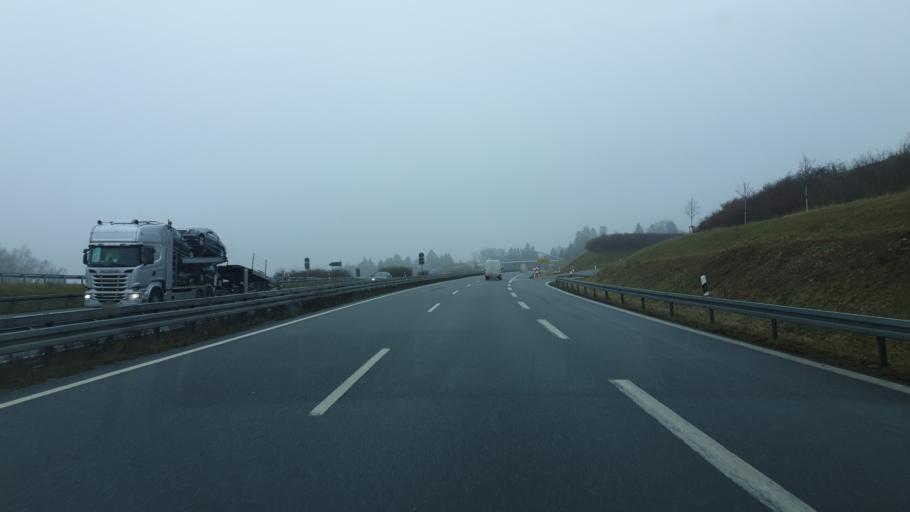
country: DE
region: Saxony
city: Hilbersdorf
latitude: 50.8013
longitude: 12.9733
